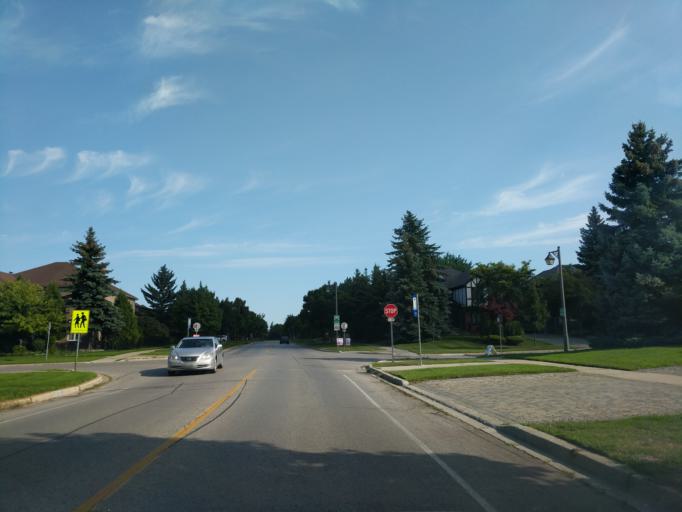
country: CA
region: Ontario
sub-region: York
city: Richmond Hill
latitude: 43.8641
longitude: -79.3992
